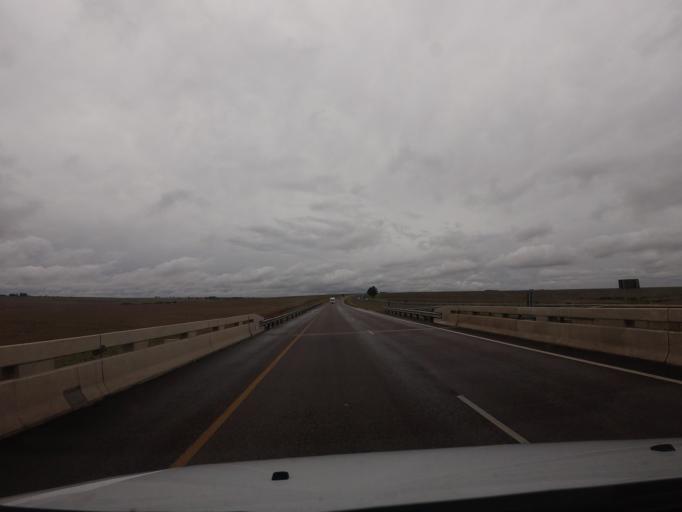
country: ZA
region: Mpumalanga
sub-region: Nkangala District Municipality
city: Middelburg
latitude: -25.8172
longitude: 29.5907
